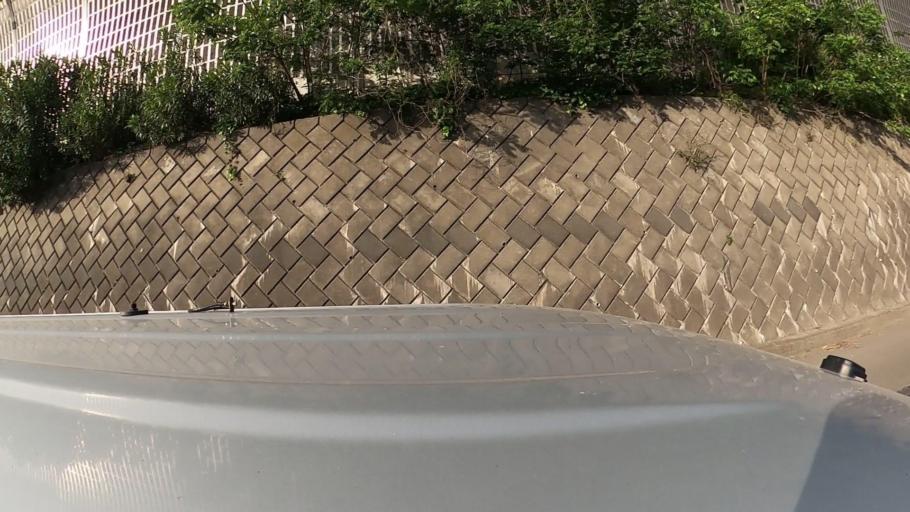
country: JP
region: Saitama
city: Asaka
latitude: 35.7884
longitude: 139.5507
